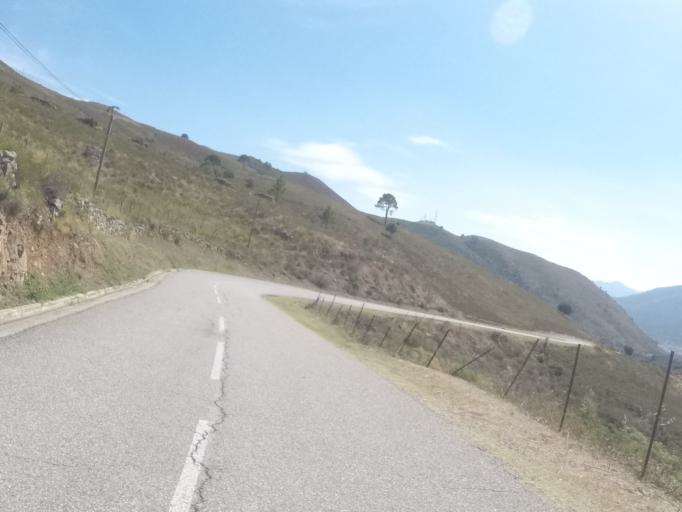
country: FR
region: Corsica
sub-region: Departement de la Haute-Corse
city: Corte
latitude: 42.3424
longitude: 9.1489
